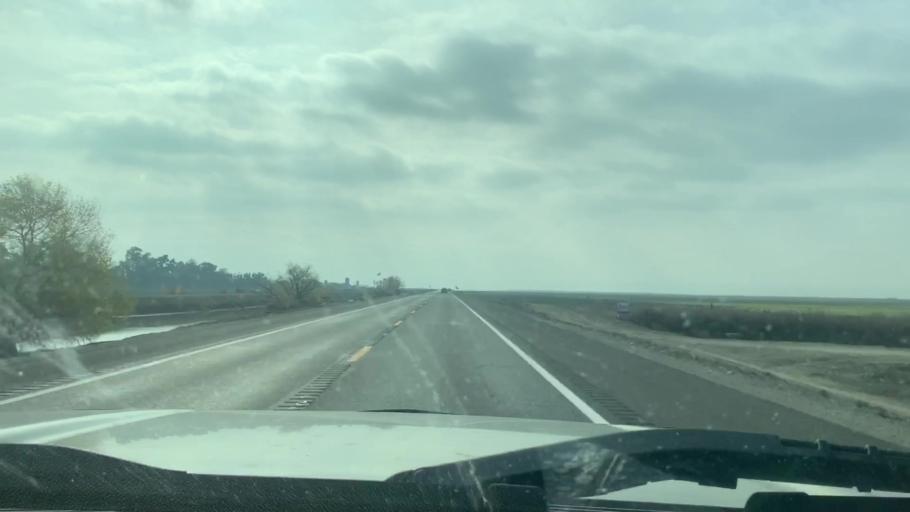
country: US
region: California
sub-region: Kings County
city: Stratford
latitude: 36.1290
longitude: -119.8869
